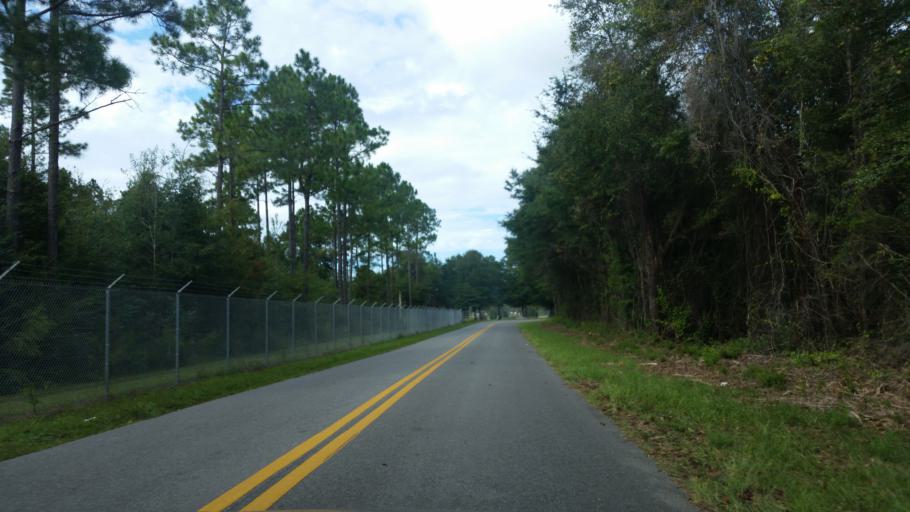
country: US
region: Florida
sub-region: Santa Rosa County
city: Point Baker
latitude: 30.7327
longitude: -87.0125
